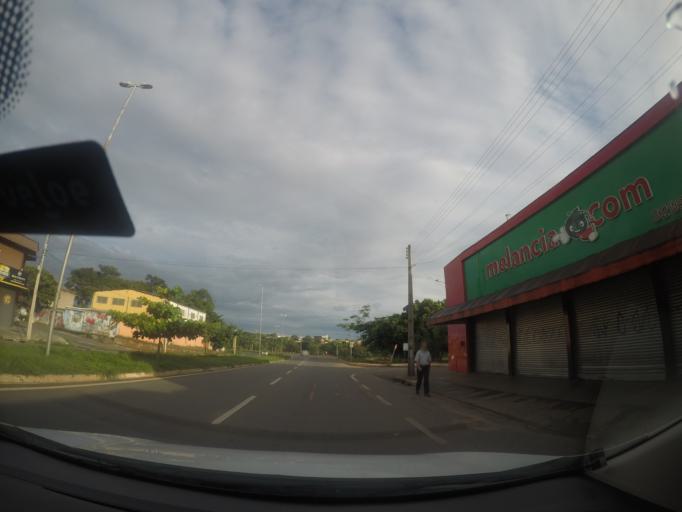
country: BR
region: Goias
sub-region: Goiania
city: Goiania
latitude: -16.6373
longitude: -49.3181
